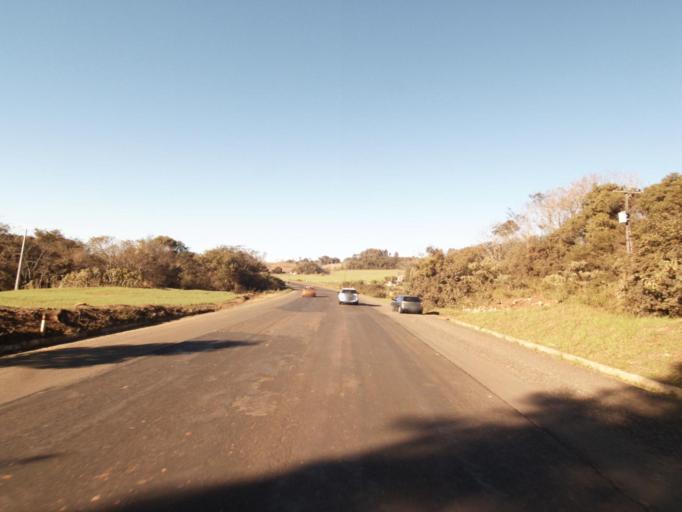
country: BR
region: Rio Grande do Sul
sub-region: Frederico Westphalen
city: Frederico Westphalen
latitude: -26.8986
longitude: -53.1908
